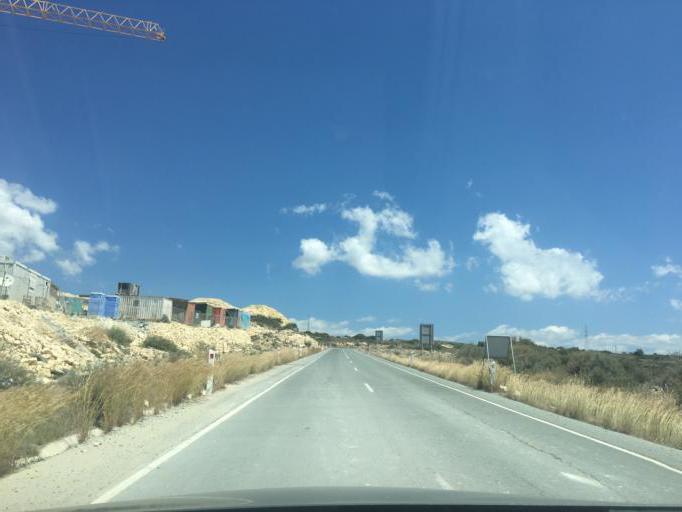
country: CY
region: Limassol
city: Mouttagiaka
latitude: 34.7294
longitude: 33.0615
